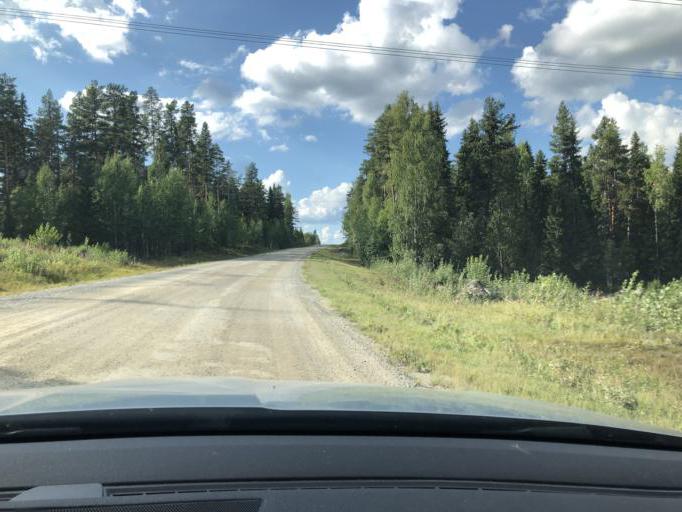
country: SE
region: Vaesternorrland
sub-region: Solleftea Kommun
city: Solleftea
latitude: 63.3140
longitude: 17.2505
